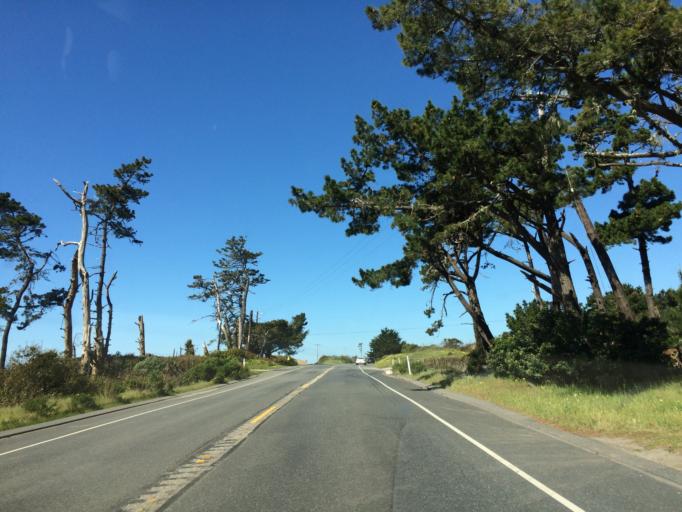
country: US
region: California
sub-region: Santa Cruz County
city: Bonny Doon
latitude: 37.1137
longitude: -122.3004
